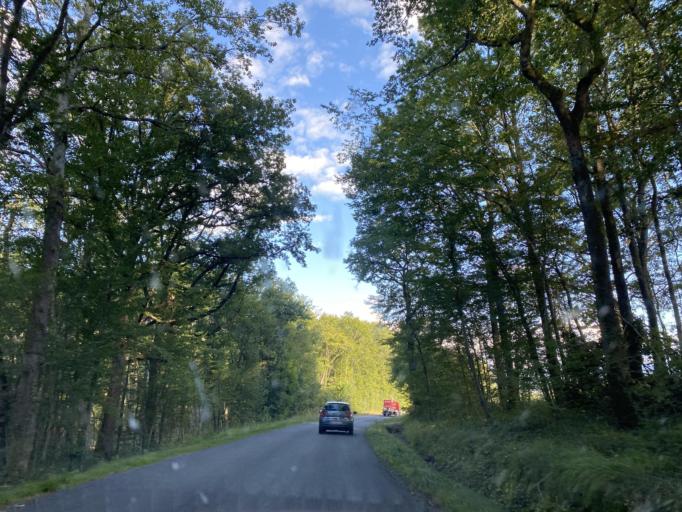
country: FR
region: Auvergne
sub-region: Departement du Puy-de-Dome
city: Saint-Sylvestre-Pragoulin
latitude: 46.0099
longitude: 3.4014
